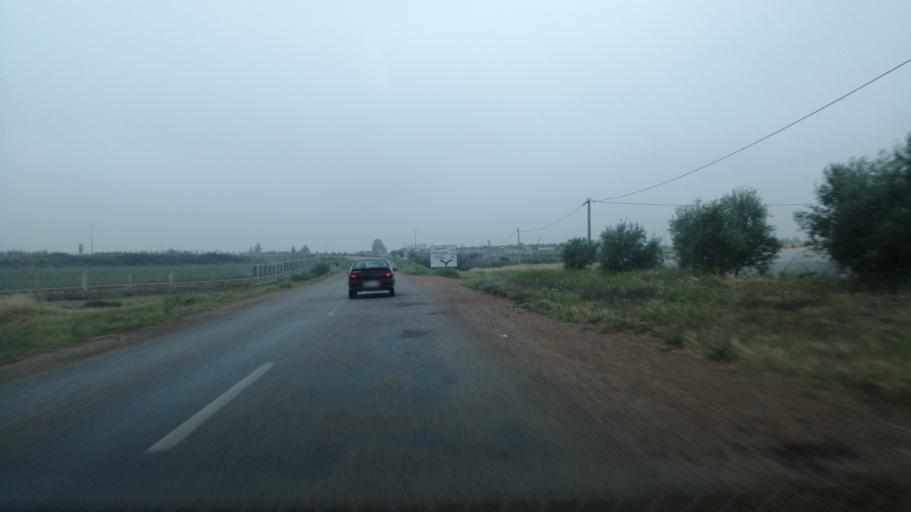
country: MA
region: Rabat-Sale-Zemmour-Zaer
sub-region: Khemisset
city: Tiflet
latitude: 33.7404
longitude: -6.2699
